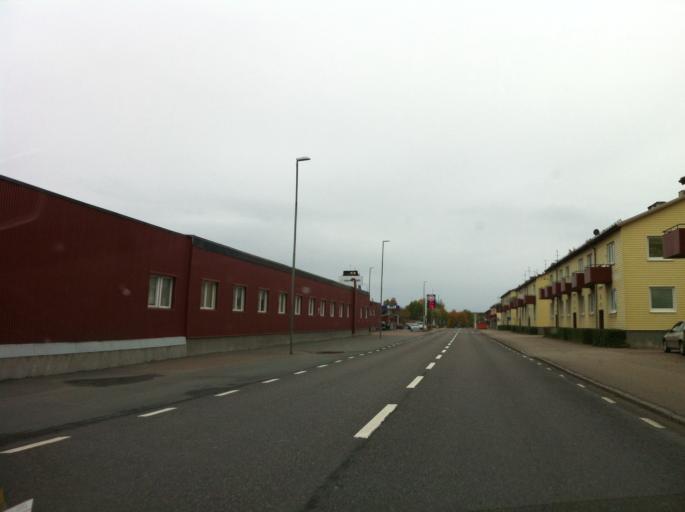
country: SE
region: Dalarna
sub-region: Ludvika Kommun
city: Grangesberg
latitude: 60.0712
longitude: 14.9998
